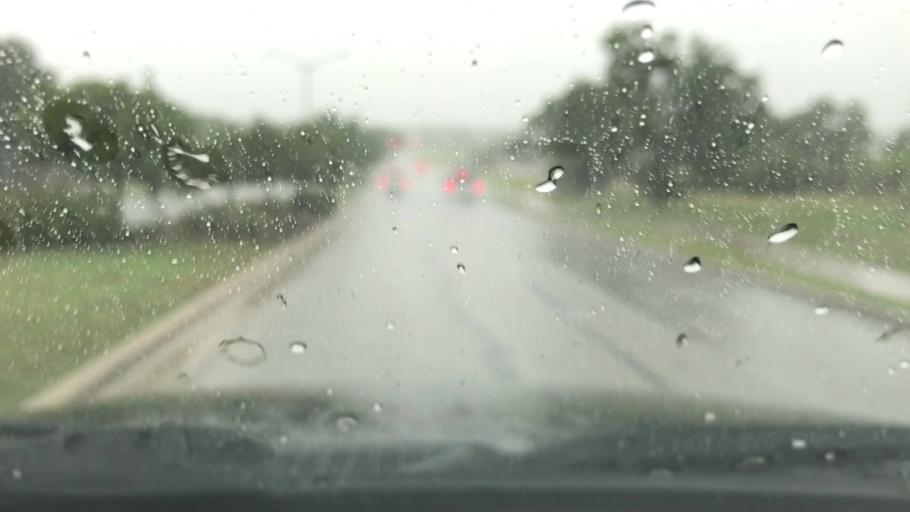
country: US
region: Texas
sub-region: Williamson County
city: Leander
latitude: 30.5401
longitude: -97.8626
